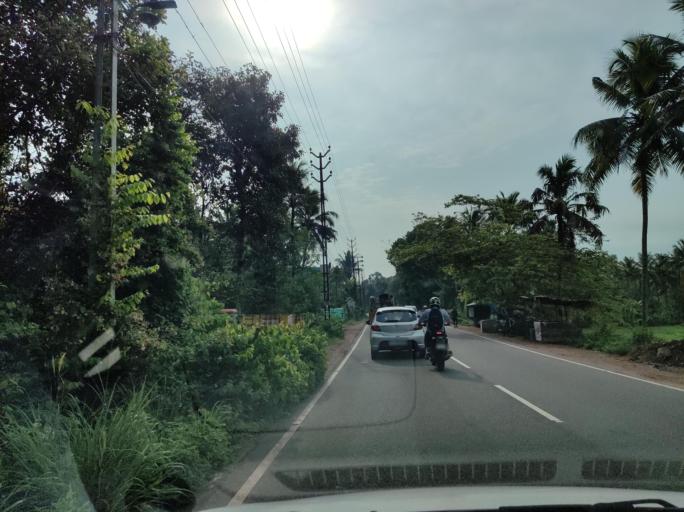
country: IN
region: Kerala
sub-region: Alappuzha
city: Kattanam
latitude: 9.1733
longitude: 76.5869
